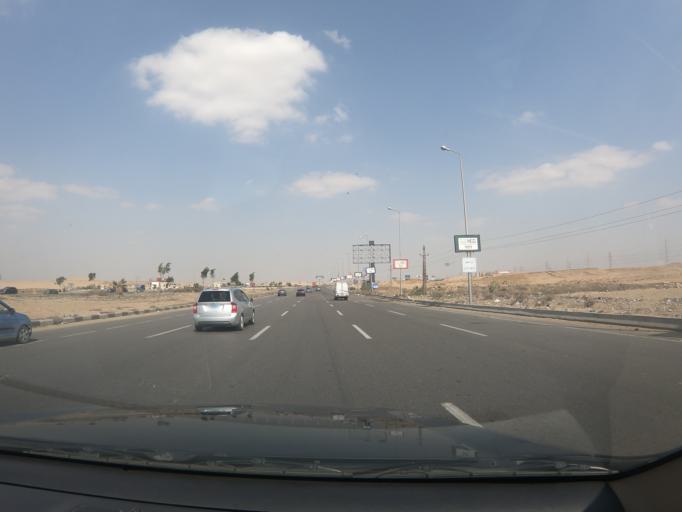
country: EG
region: Muhafazat al Qalyubiyah
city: Al Khankah
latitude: 30.0860
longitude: 31.4881
